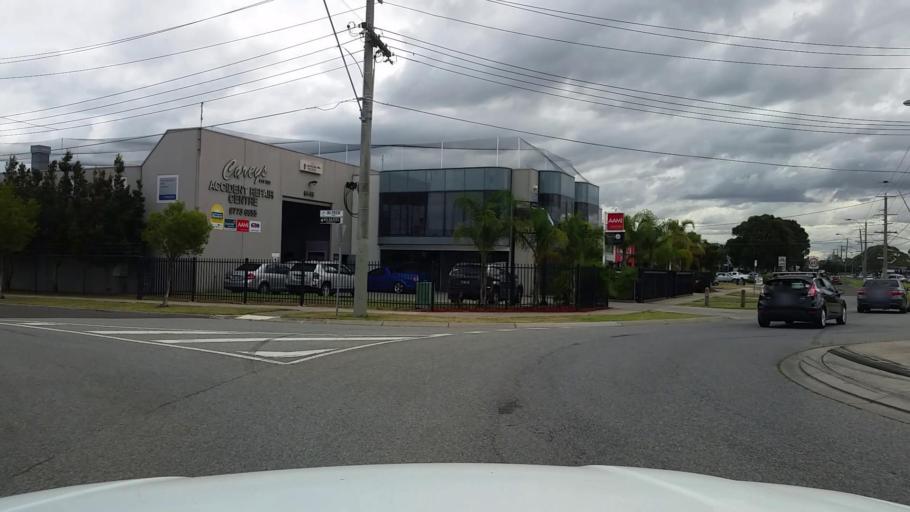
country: AU
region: Victoria
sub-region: Frankston
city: Frankston North
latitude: -38.1168
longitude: 145.1407
